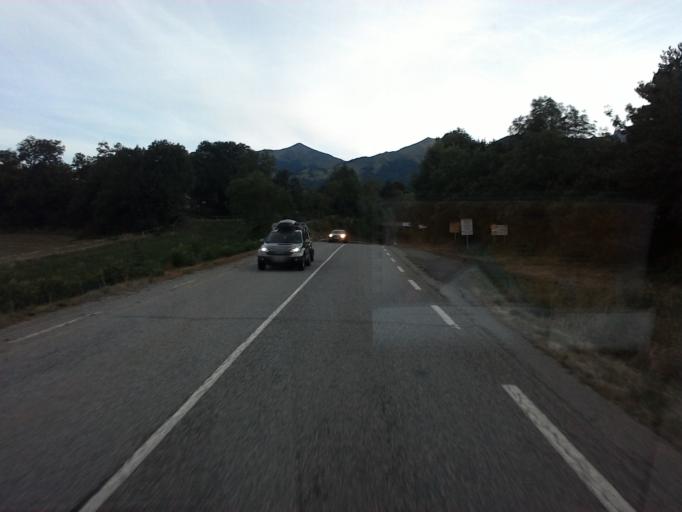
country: FR
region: Provence-Alpes-Cote d'Azur
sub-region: Departement des Hautes-Alpes
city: Saint-Bonnet-en-Champsaur
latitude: 44.7664
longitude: 6.0133
